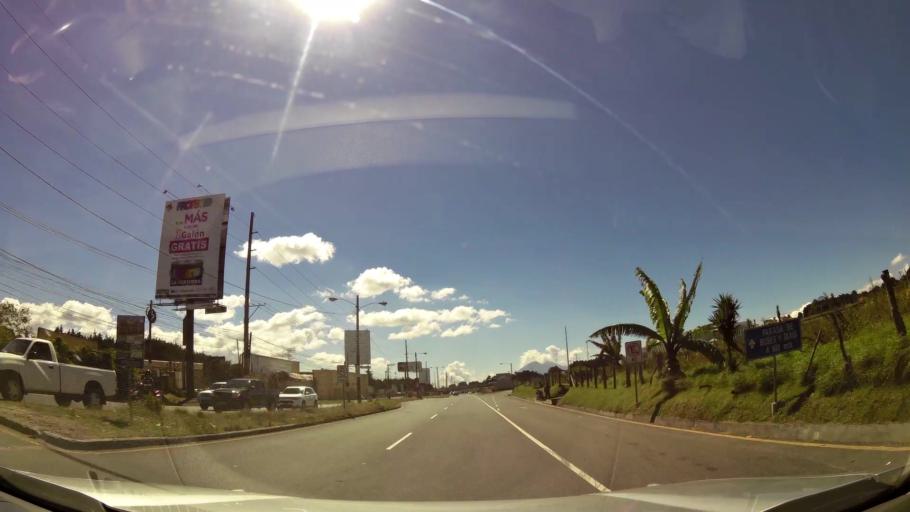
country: GT
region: Guatemala
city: Santa Catarina Pinula
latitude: 14.5132
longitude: -90.4759
